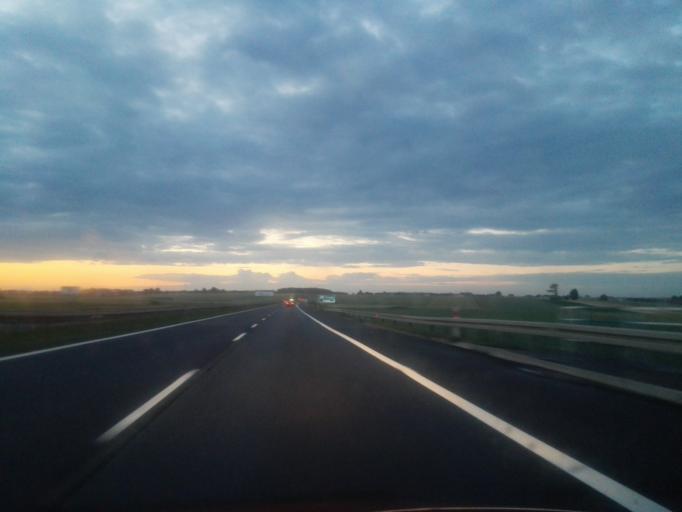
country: PL
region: Lodz Voivodeship
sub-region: Powiat piotrkowski
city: Grabica
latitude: 51.5205
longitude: 19.5999
